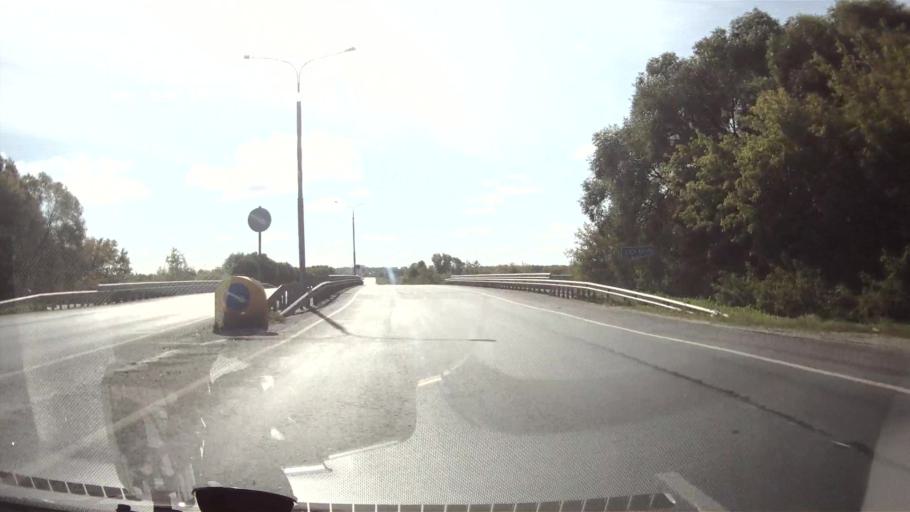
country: RU
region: Ulyanovsk
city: Isheyevka
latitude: 54.3047
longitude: 48.2420
